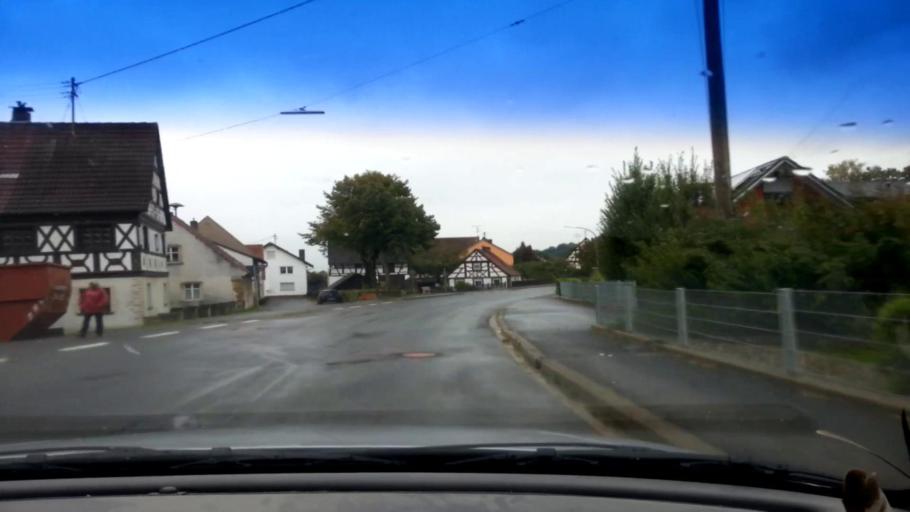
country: DE
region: Bavaria
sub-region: Upper Franconia
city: Poxdorf
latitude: 49.9792
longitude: 11.0888
